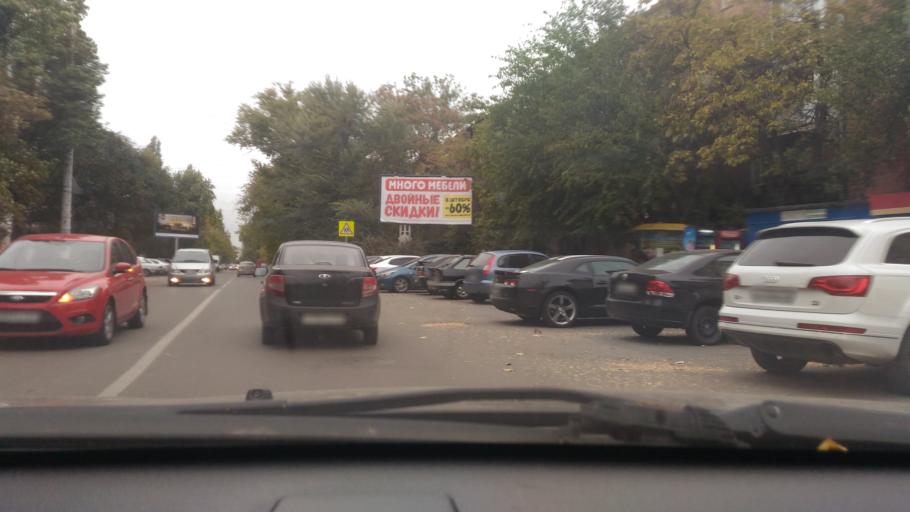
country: RU
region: Rostov
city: Rostov-na-Donu
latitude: 47.2365
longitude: 39.7111
